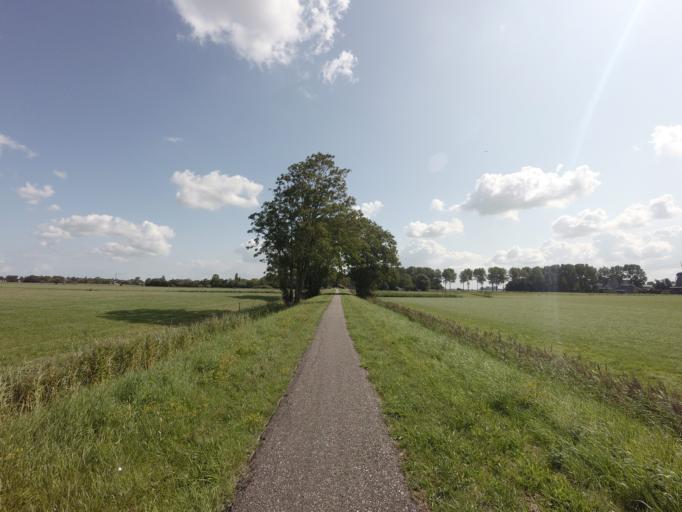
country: NL
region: Friesland
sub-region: Gemeente Leeuwarderadeel
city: Stiens
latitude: 53.2830
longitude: 5.7181
